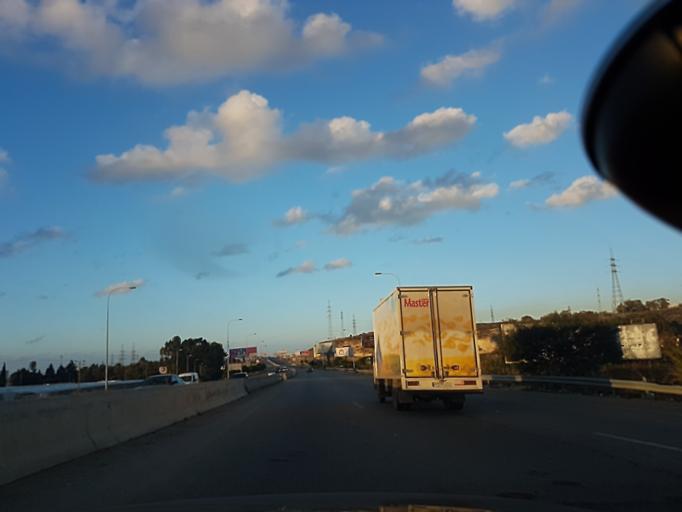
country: LB
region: Liban-Sud
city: Sidon
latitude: 33.4883
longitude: 35.3417
